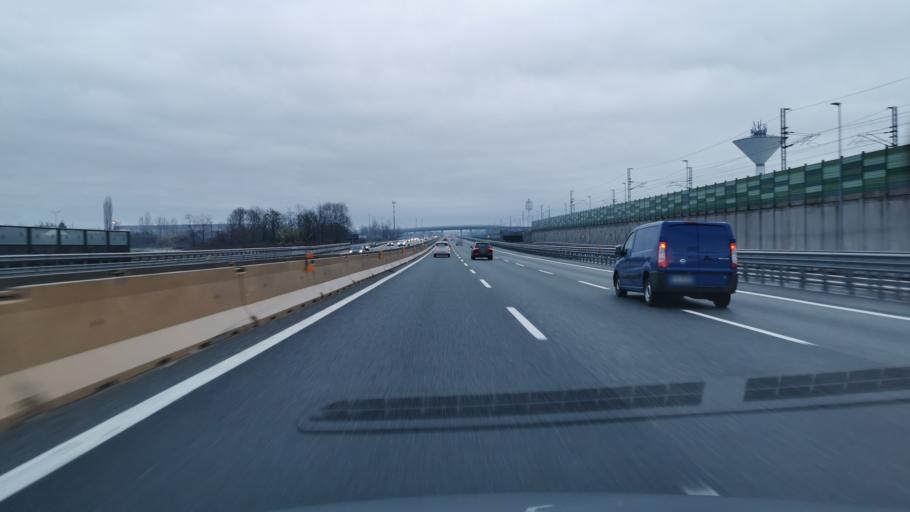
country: IT
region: Piedmont
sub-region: Provincia di Torino
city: Chivasso
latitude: 45.2051
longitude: 7.8819
